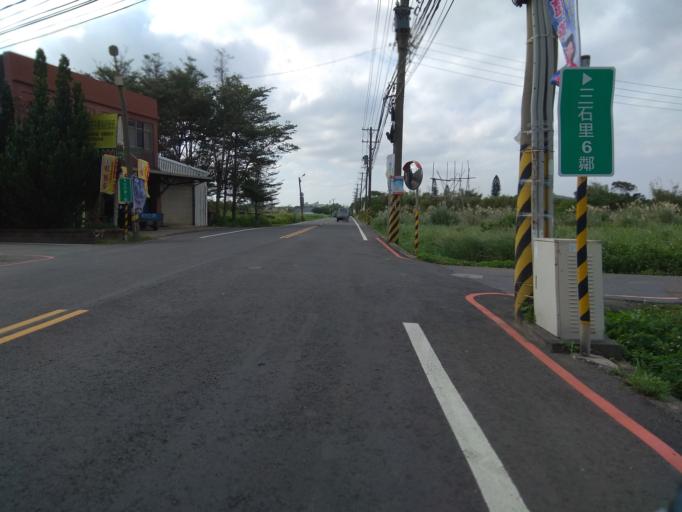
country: TW
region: Taiwan
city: Taoyuan City
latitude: 25.0699
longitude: 121.2457
